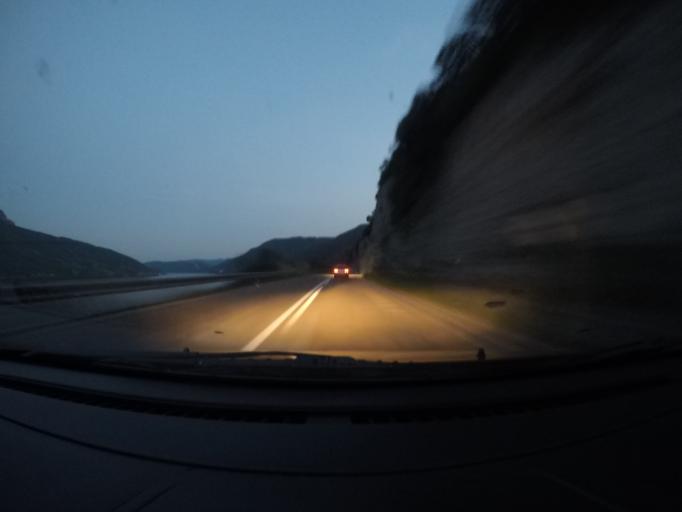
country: RO
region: Caras-Severin
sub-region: Comuna Berzasca
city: Berzasca
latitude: 44.5871
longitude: 22.0219
